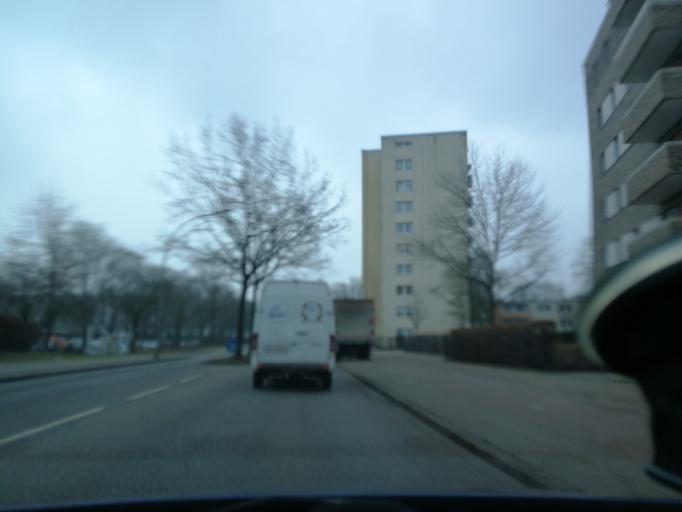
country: DE
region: Lower Saxony
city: Neu Wulmstorf
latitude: 53.4779
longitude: 9.8799
